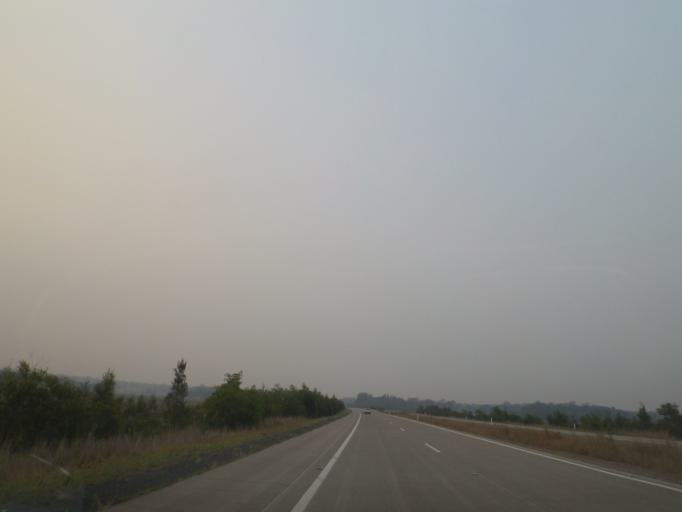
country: AU
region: New South Wales
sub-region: Kempsey
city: Frederickton
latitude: -30.9717
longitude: 152.8590
